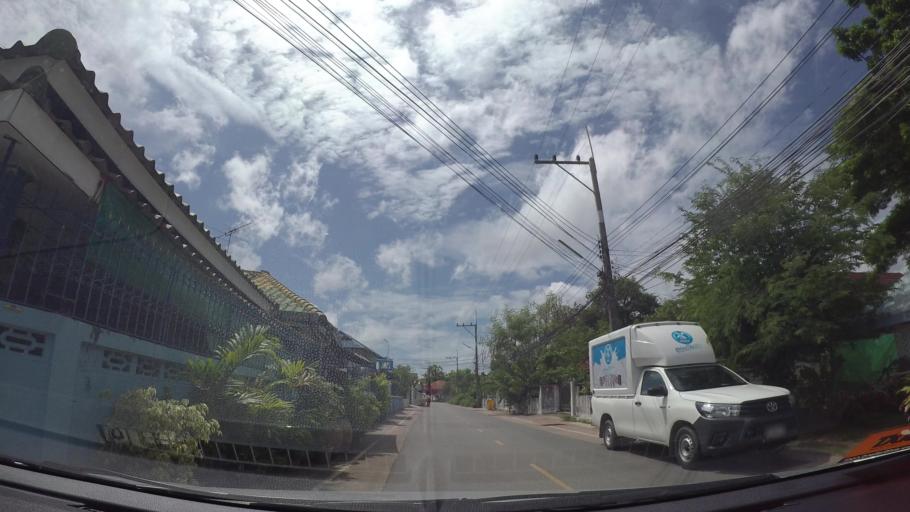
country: TH
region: Chon Buri
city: Sattahip
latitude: 12.6824
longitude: 100.9063
